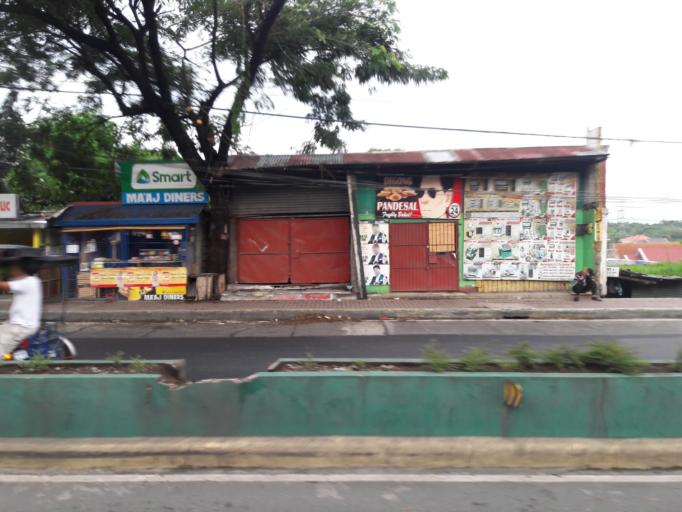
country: PH
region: Calabarzon
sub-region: Province of Cavite
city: Biga
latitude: 14.2918
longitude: 120.9586
